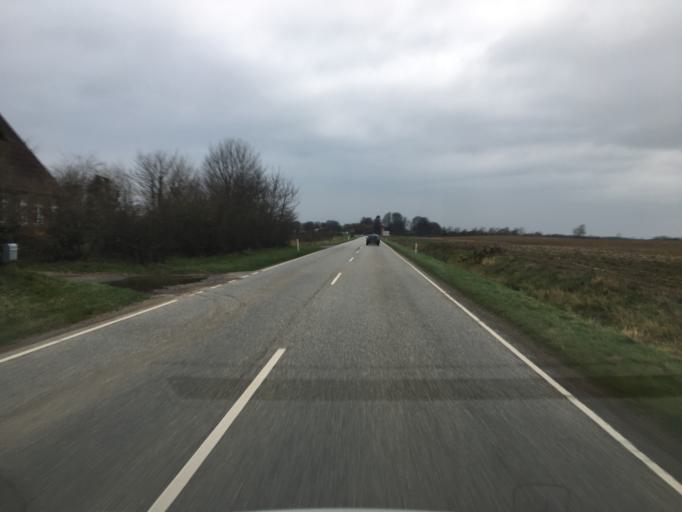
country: DK
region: South Denmark
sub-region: Aabenraa Kommune
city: Tinglev
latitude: 55.0092
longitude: 9.2632
